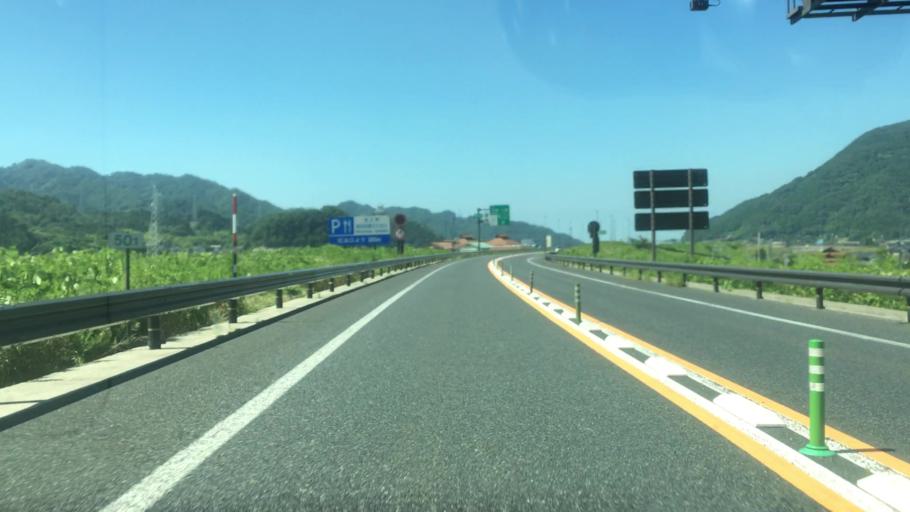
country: JP
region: Tottori
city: Tottori
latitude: 35.3894
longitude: 134.2034
